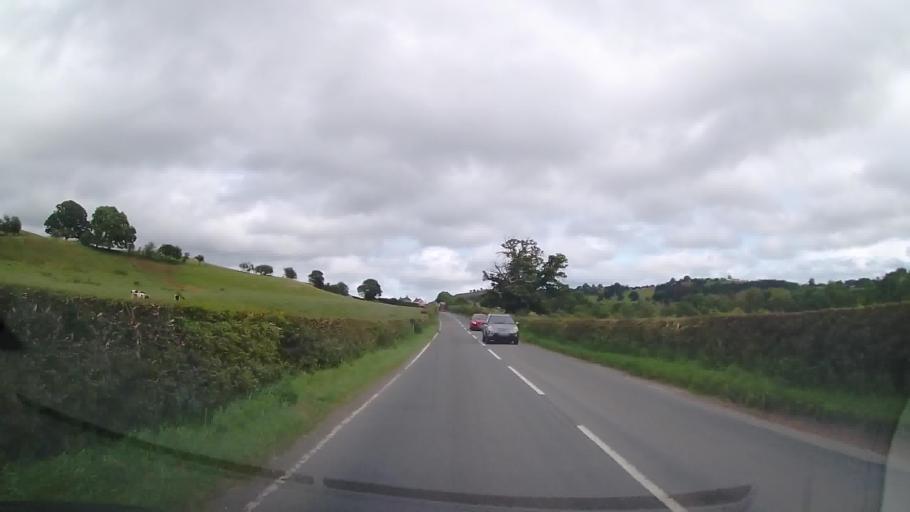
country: GB
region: Wales
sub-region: Sir Powys
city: Llanfechain
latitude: 52.8055
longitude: -3.1779
